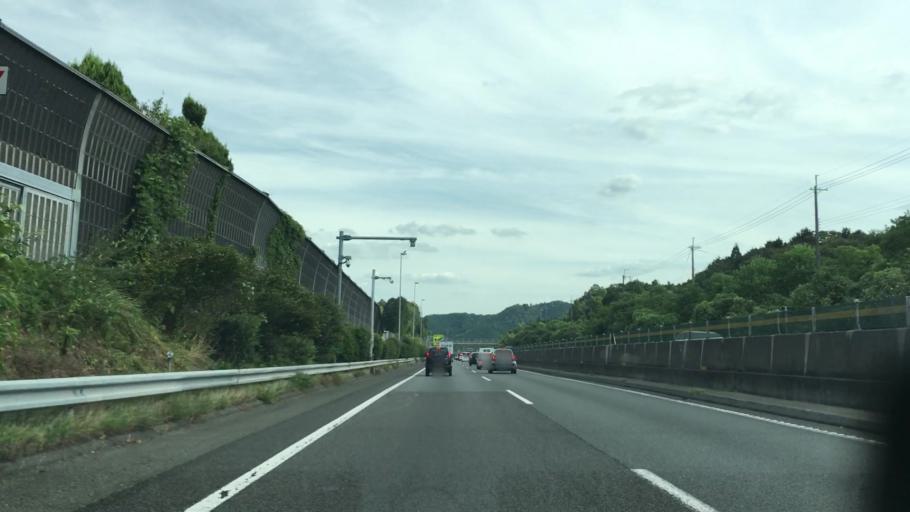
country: JP
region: Shiga Prefecture
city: Otsu-shi
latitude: 34.9860
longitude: 135.8796
